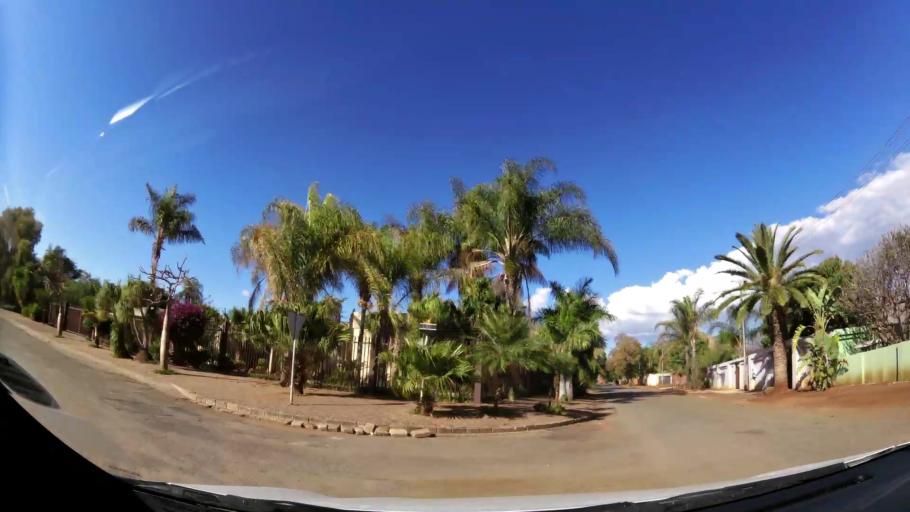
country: ZA
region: Limpopo
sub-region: Waterberg District Municipality
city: Mokopane
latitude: -24.1773
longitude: 28.9957
